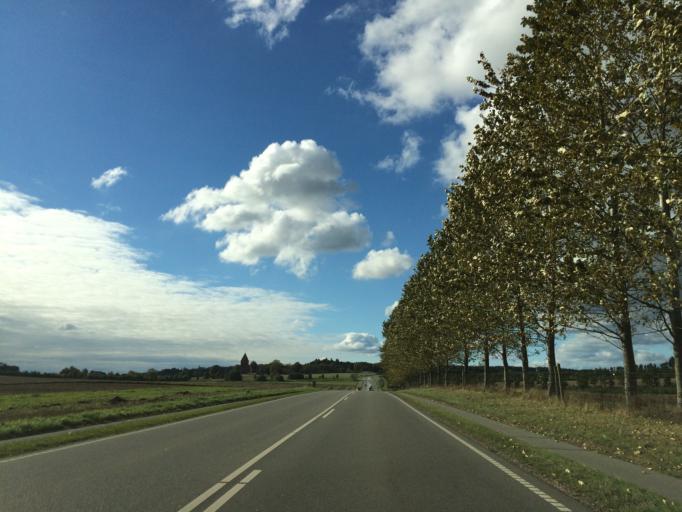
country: DK
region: Central Jutland
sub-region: Skanderborg Kommune
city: Ry
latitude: 56.0814
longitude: 9.7172
